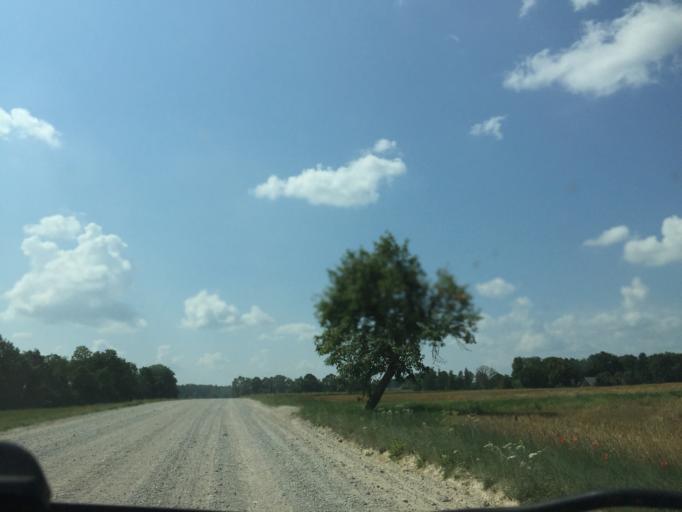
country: LV
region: Tervete
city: Zelmeni
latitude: 56.3926
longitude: 23.3149
